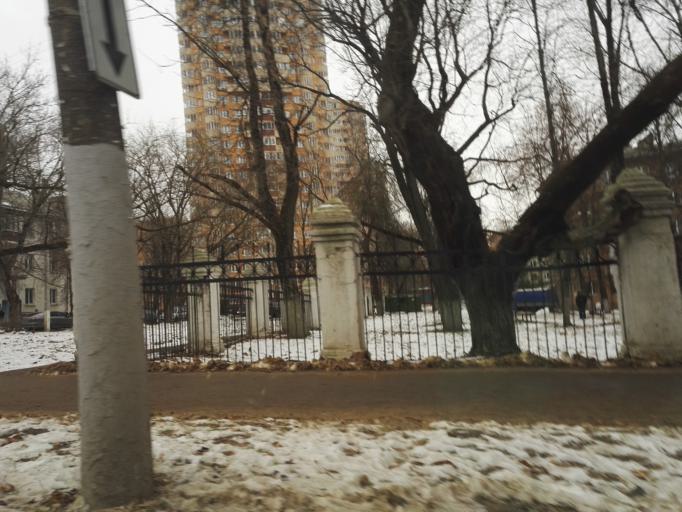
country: RU
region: Tula
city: Tula
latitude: 54.1747
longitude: 37.6114
